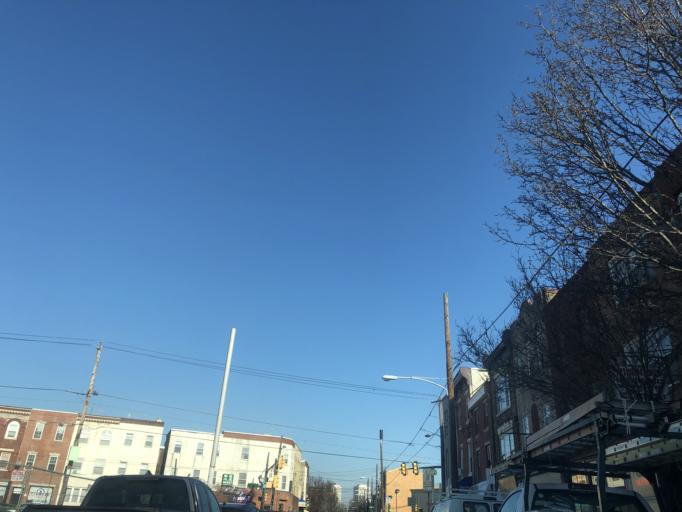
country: US
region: Pennsylvania
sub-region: Philadelphia County
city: Philadelphia
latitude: 39.9354
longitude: -75.1568
